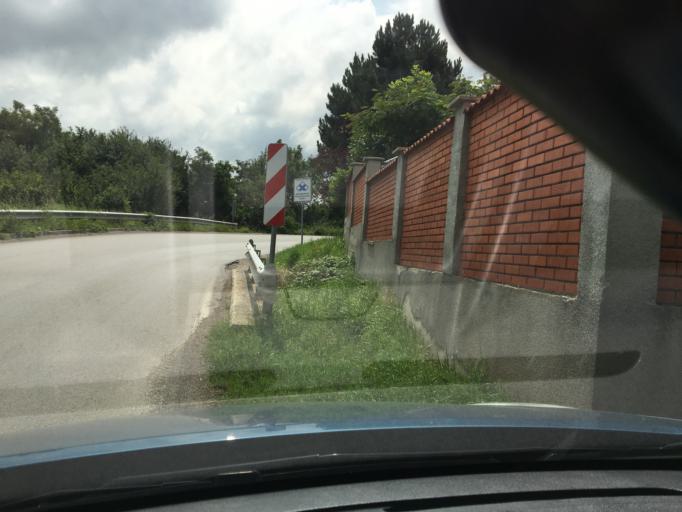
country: BG
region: Sofia-Capital
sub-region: Stolichna Obshtina
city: Sofia
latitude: 42.6044
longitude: 23.3675
